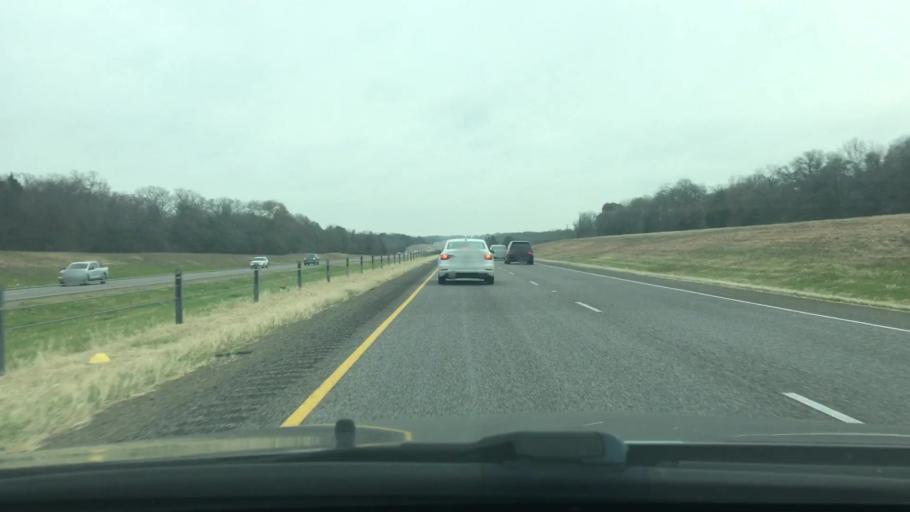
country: US
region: Texas
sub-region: Freestone County
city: Fairfield
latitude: 31.7561
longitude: -96.2053
